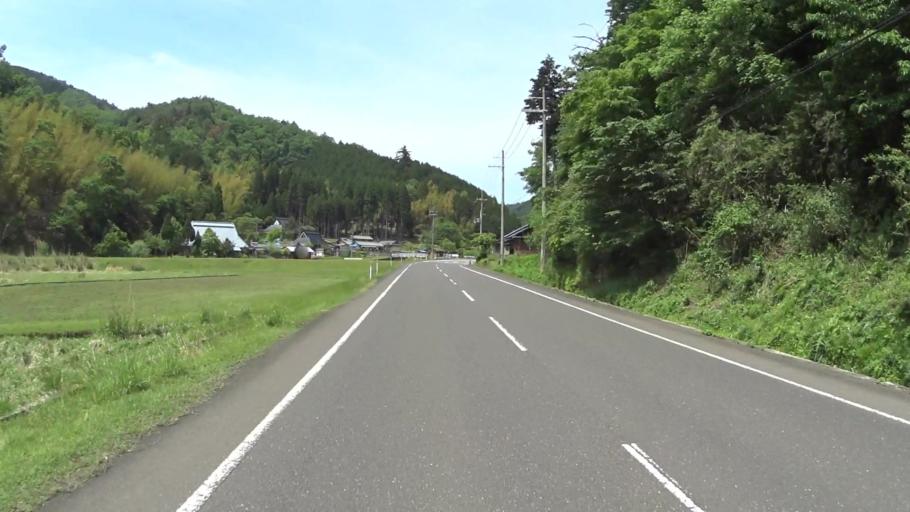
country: JP
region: Kyoto
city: Maizuru
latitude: 35.3993
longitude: 135.4627
